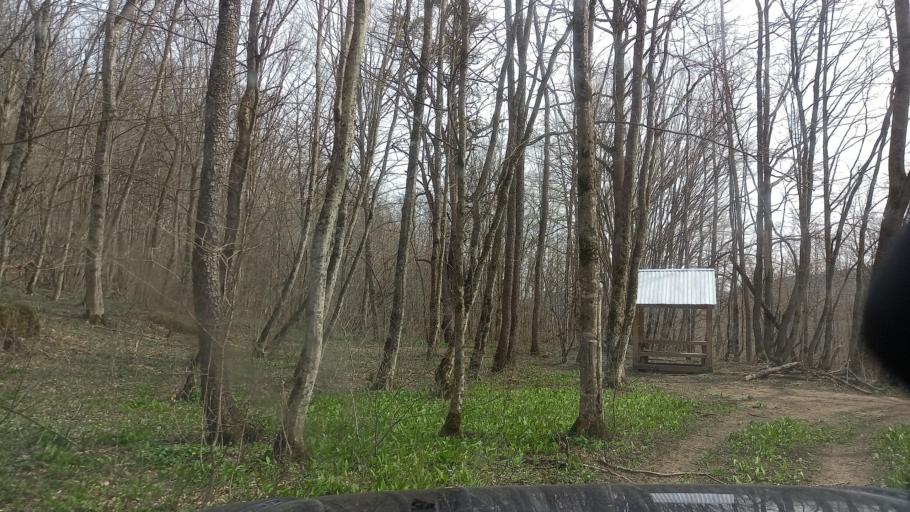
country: RU
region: Adygeya
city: Kamennomostskiy
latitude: 44.1115
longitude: 40.1034
